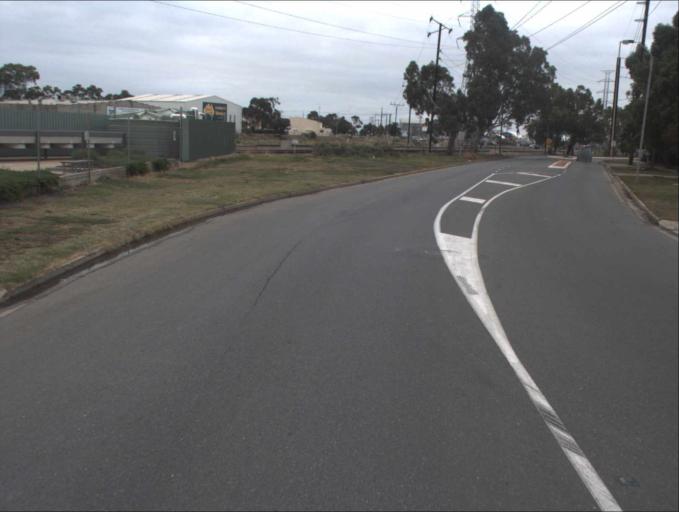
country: AU
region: South Australia
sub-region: Port Adelaide Enfield
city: Blair Athol
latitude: -34.8426
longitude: 138.5820
